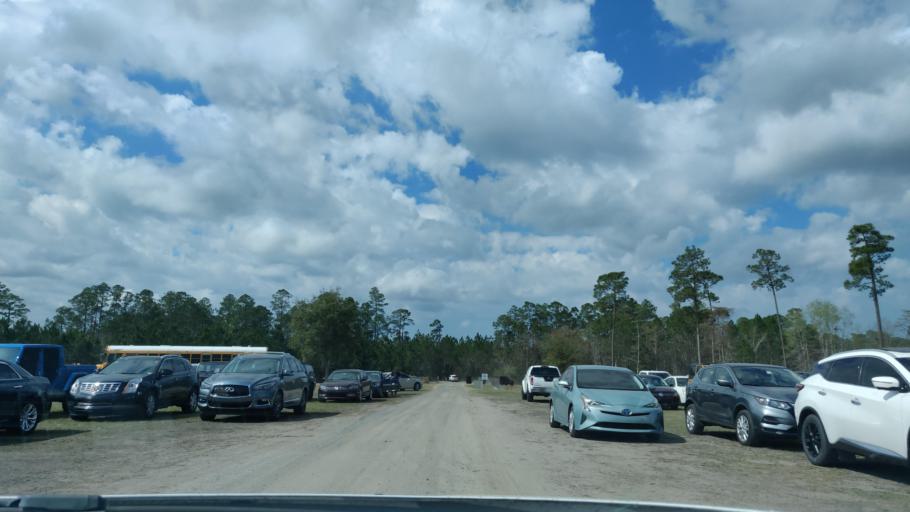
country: US
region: Florida
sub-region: Duval County
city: Baldwin
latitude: 30.3394
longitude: -81.9045
